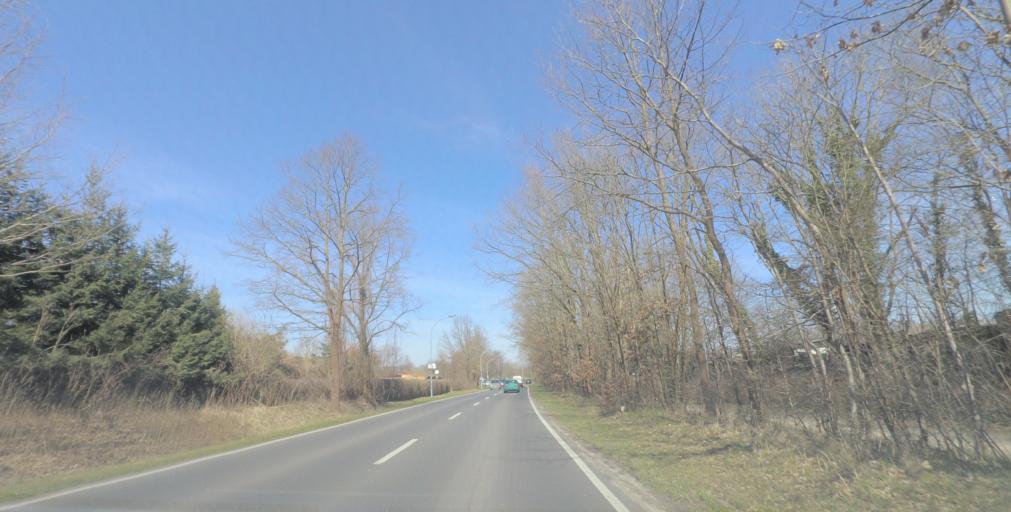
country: DE
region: Brandenburg
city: Neuruppin
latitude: 52.9006
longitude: 12.8000
